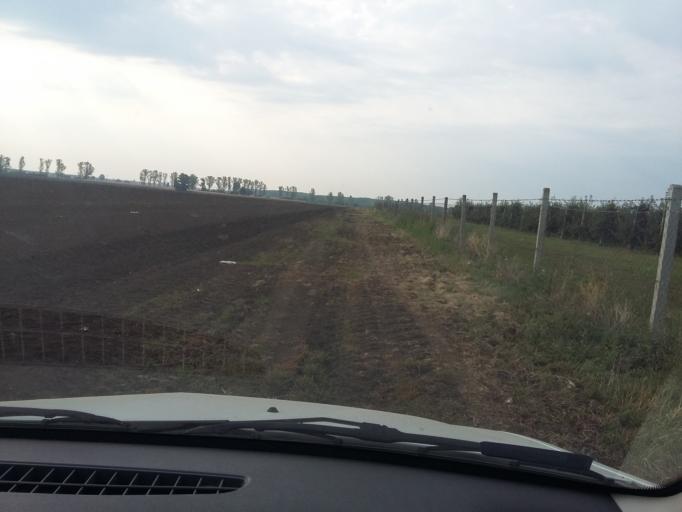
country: HU
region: Borsod-Abauj-Zemplen
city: Taktaharkany
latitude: 48.1261
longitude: 21.1073
